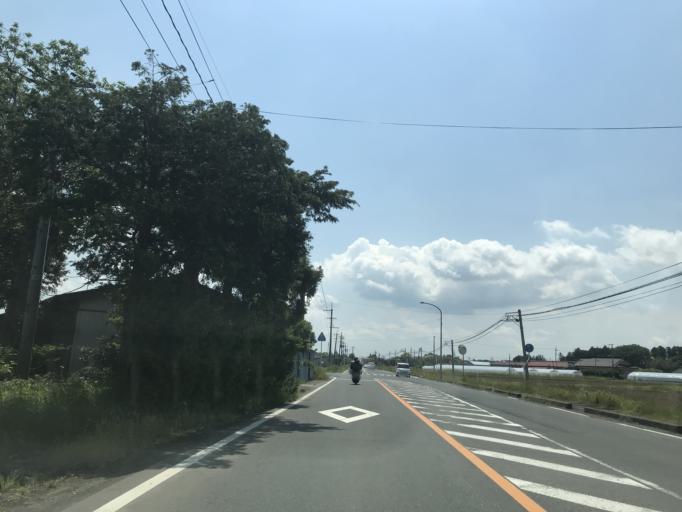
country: JP
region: Miyagi
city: Kogota
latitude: 38.5686
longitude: 141.0426
